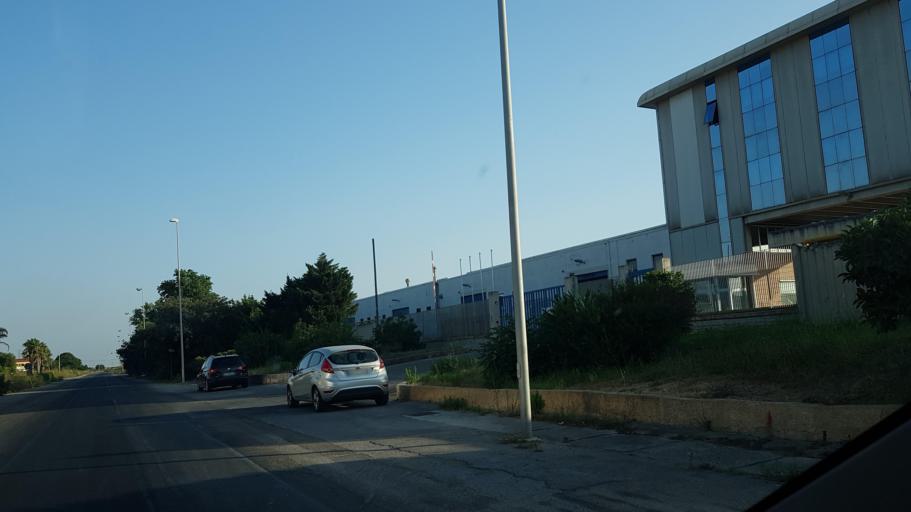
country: IT
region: Apulia
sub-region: Provincia di Brindisi
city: Materdomini
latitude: 40.6307
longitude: 17.9747
